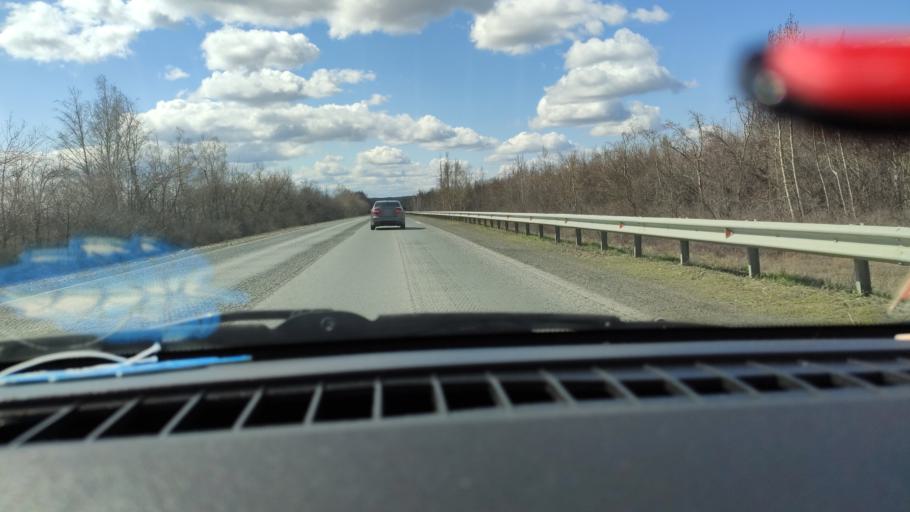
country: RU
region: Saratov
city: Dukhovnitskoye
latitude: 52.6701
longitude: 48.2207
